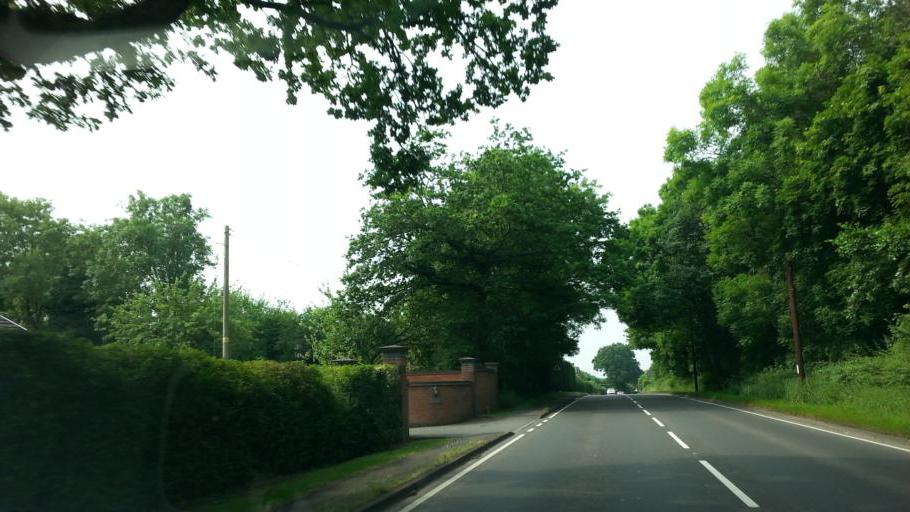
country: GB
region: England
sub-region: Warwickshire
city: Studley
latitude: 52.2939
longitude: -1.8824
